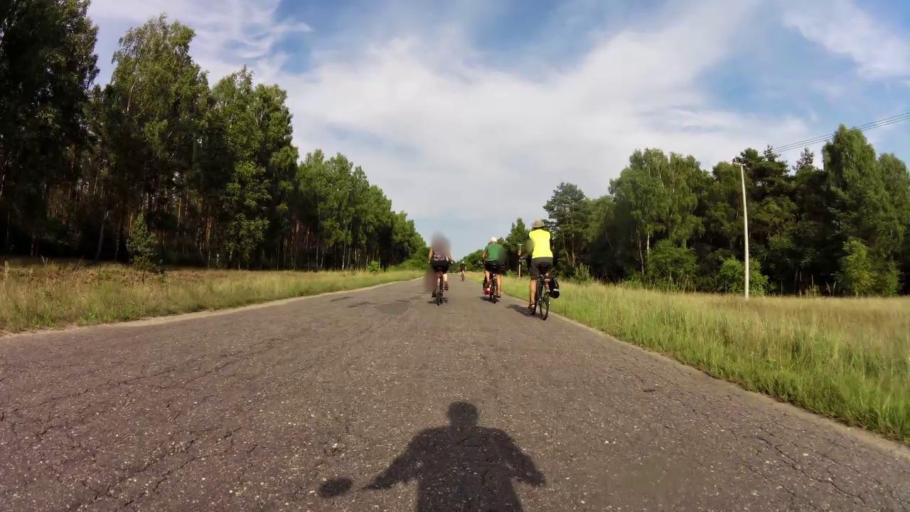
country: PL
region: West Pomeranian Voivodeship
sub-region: Powiat drawski
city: Drawsko Pomorskie
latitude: 53.4708
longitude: 15.7062
